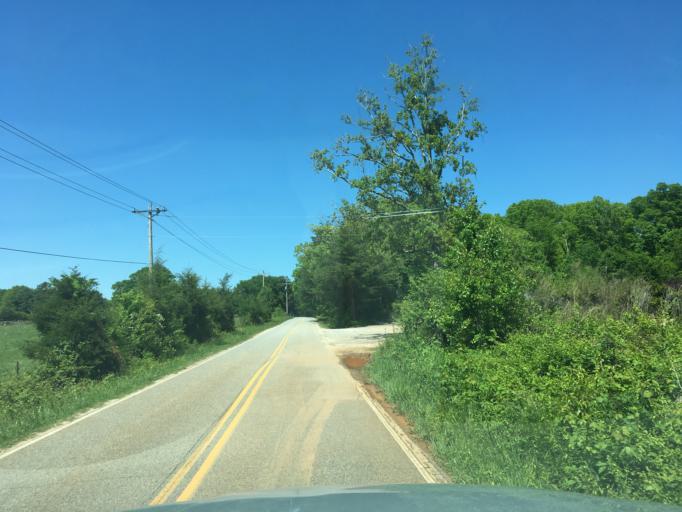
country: US
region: South Carolina
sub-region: Spartanburg County
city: Duncan
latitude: 34.8738
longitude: -82.1779
